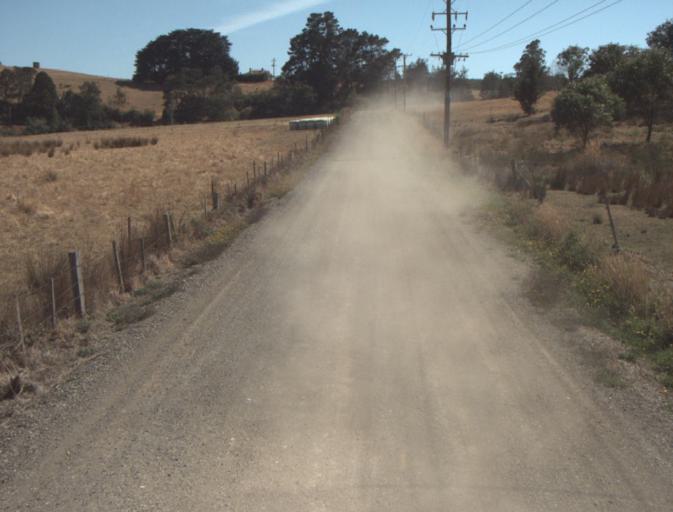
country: AU
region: Tasmania
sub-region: Launceston
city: Mayfield
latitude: -41.2262
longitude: 147.2366
